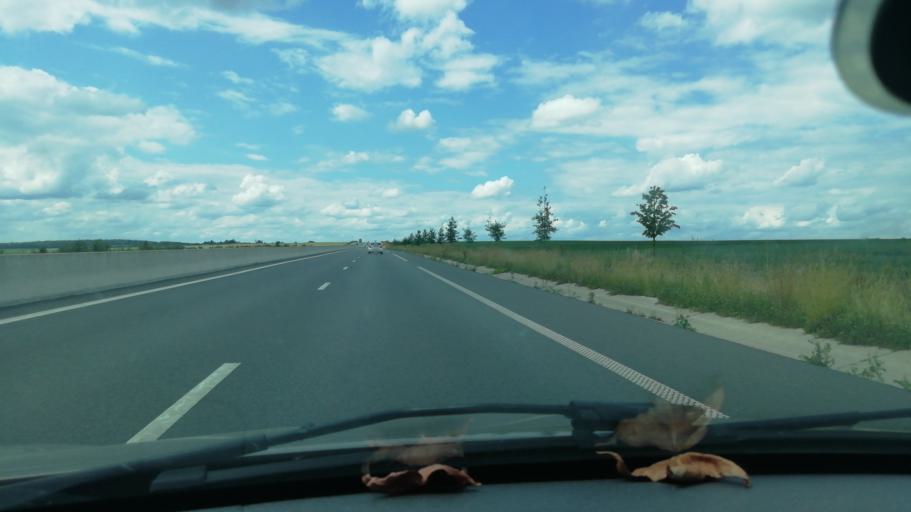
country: FR
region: Nord-Pas-de-Calais
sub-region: Departement du Pas-de-Calais
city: Duisans
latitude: 50.3204
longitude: 2.6710
